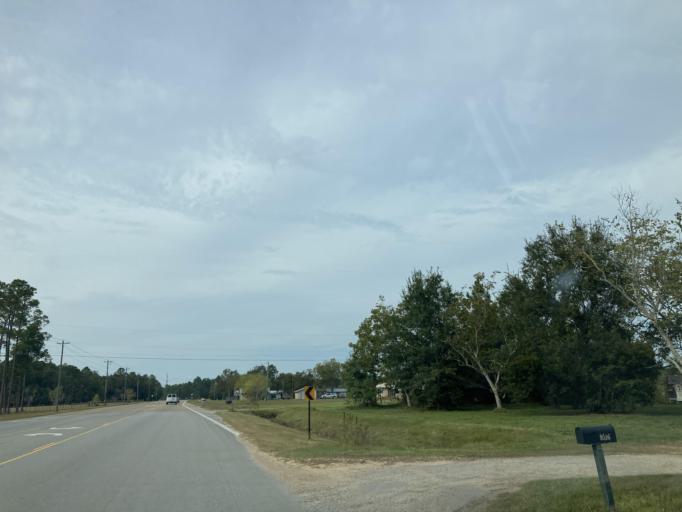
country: US
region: Mississippi
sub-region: Jackson County
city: Saint Martin
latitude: 30.4799
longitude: -88.8509
